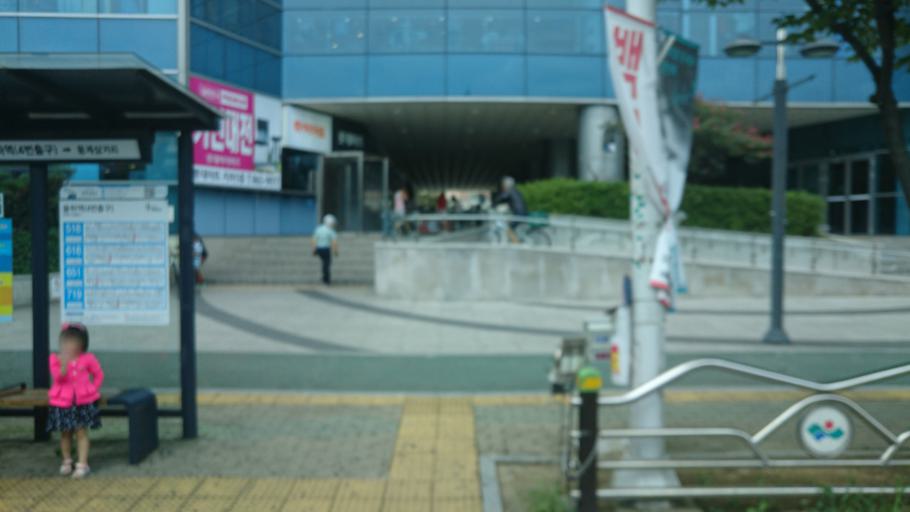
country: KR
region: Gyeongsangbuk-do
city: Gyeongsan-si
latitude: 35.8683
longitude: 128.6937
